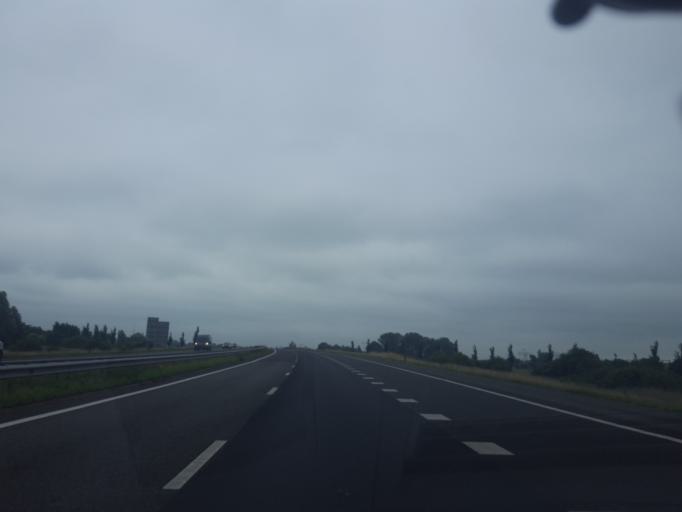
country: NL
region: Friesland
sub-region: Gemeente Boarnsterhim
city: Nes
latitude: 53.0333
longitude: 5.8517
